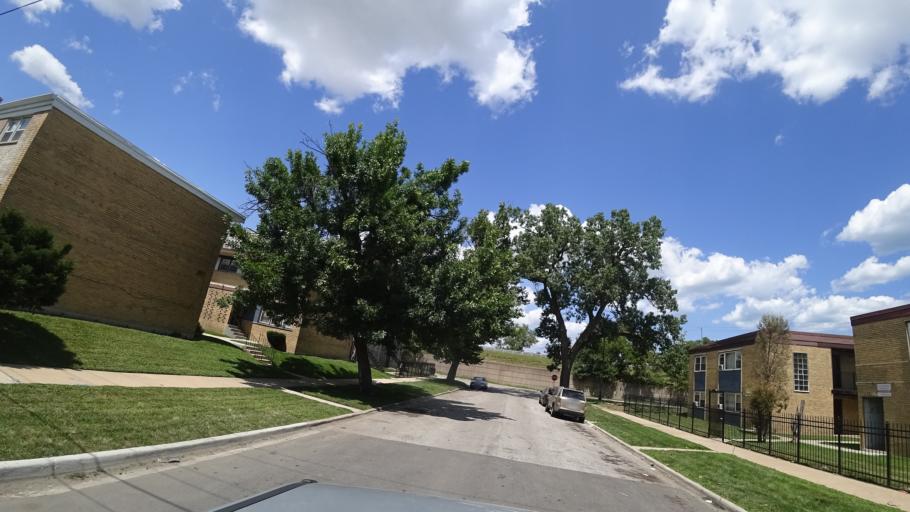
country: US
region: Illinois
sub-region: Cook County
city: Chicago
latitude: 41.7741
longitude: -87.6228
